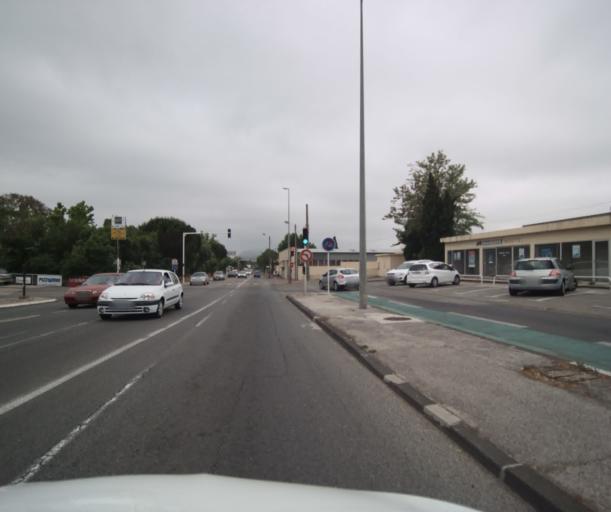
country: FR
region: Provence-Alpes-Cote d'Azur
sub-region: Departement du Var
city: La Seyne-sur-Mer
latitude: 43.1250
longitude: 5.8965
